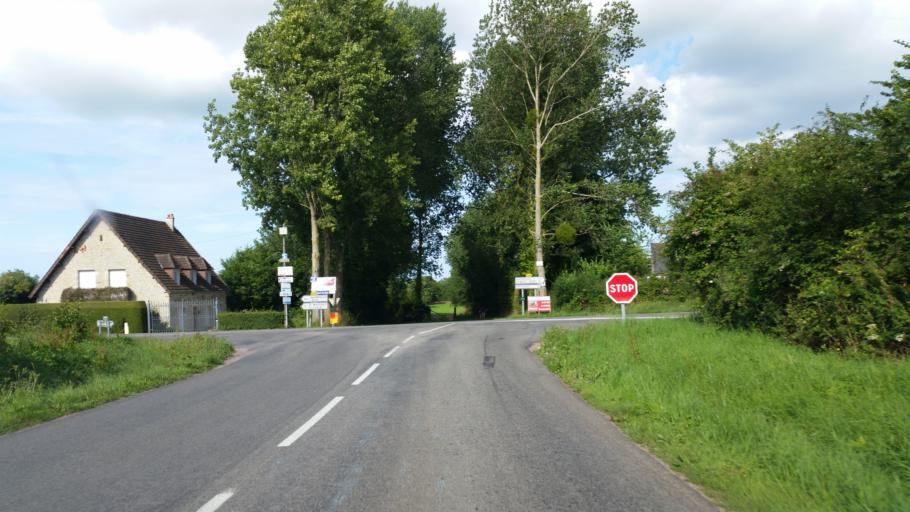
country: FR
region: Lower Normandy
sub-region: Departement de la Manche
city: Sainte-Mere-Eglise
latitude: 49.4539
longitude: -1.2688
